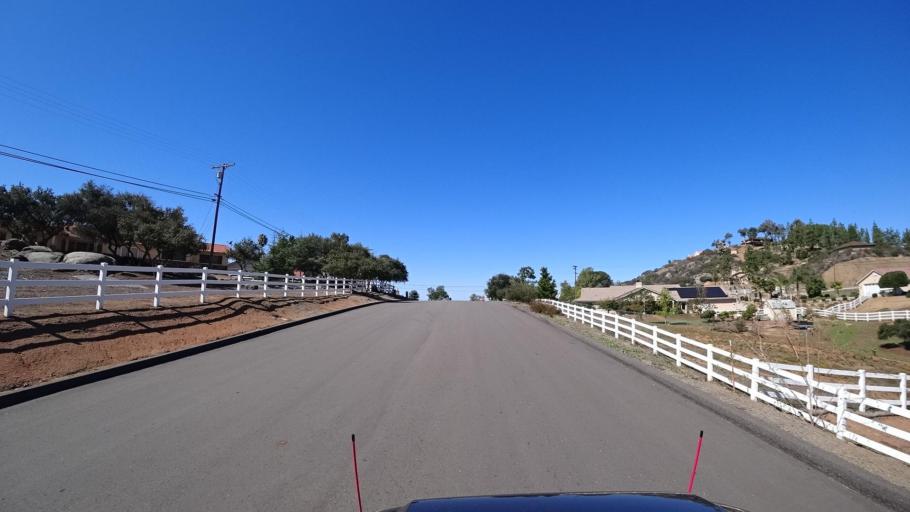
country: US
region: California
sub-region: San Diego County
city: Alpine
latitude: 32.8378
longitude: -116.7470
